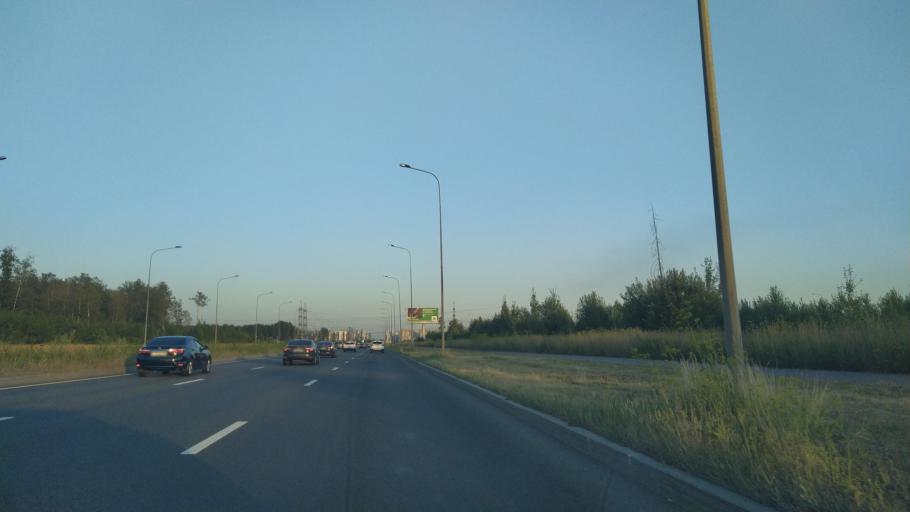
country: RU
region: St.-Petersburg
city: Levashovo
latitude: 60.0687
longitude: 30.1876
